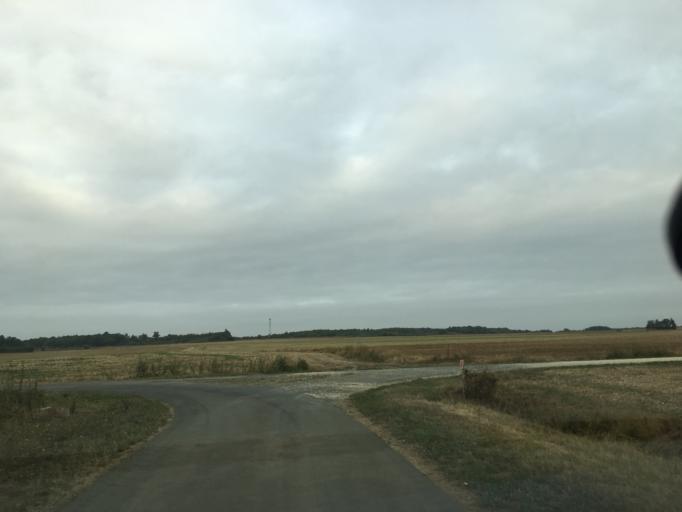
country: FR
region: Poitou-Charentes
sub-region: Departement des Deux-Sevres
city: Beauvoir-sur-Niort
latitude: 46.0890
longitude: -0.5227
